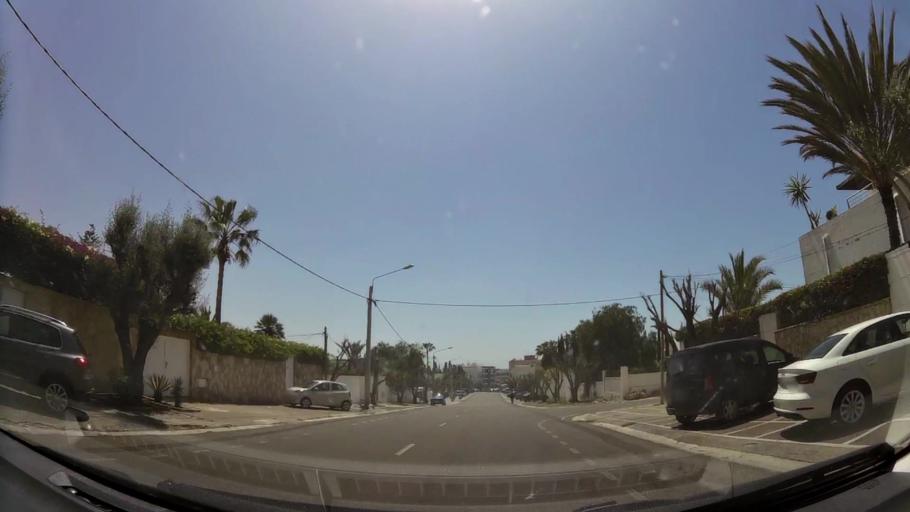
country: MA
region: Souss-Massa-Draa
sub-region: Agadir-Ida-ou-Tnan
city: Agadir
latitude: 30.4256
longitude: -9.6026
